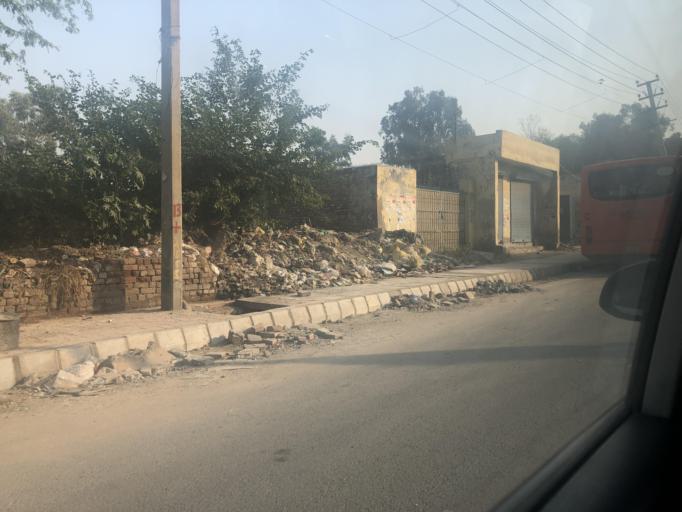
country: IN
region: Haryana
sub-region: Jhajjar
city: Bahadurgarh
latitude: 28.6175
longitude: 76.9753
